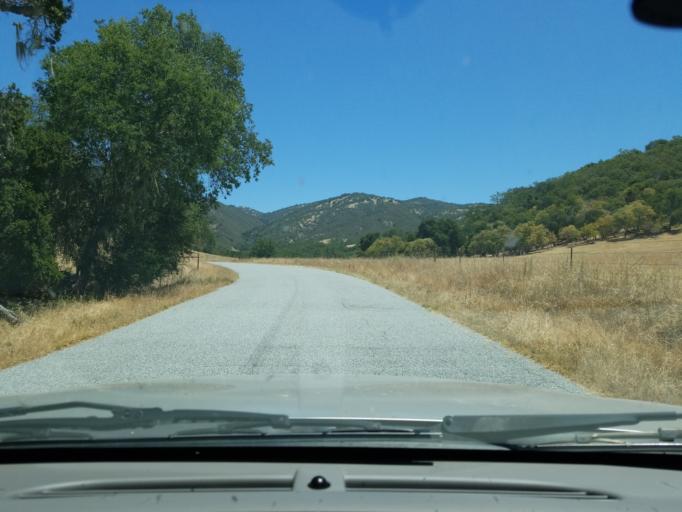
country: US
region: California
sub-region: Monterey County
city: Gonzales
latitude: 36.3880
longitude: -121.5701
